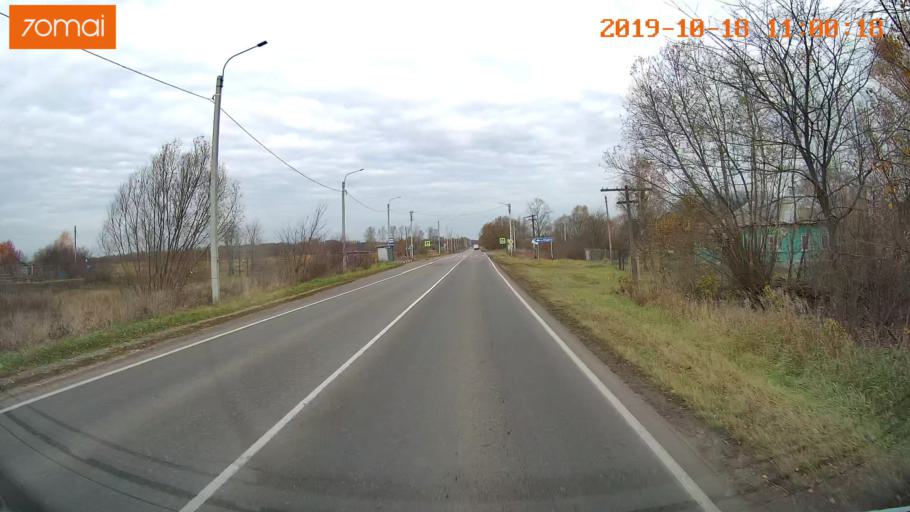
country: RU
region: Tula
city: Yepifan'
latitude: 53.8415
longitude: 38.5527
